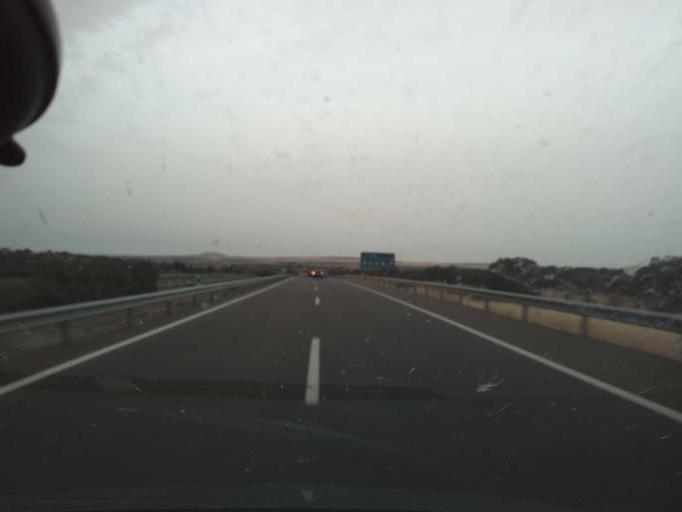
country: ES
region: Extremadura
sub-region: Provincia de Badajoz
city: Trujillanos
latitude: 38.9518
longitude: -6.2306
